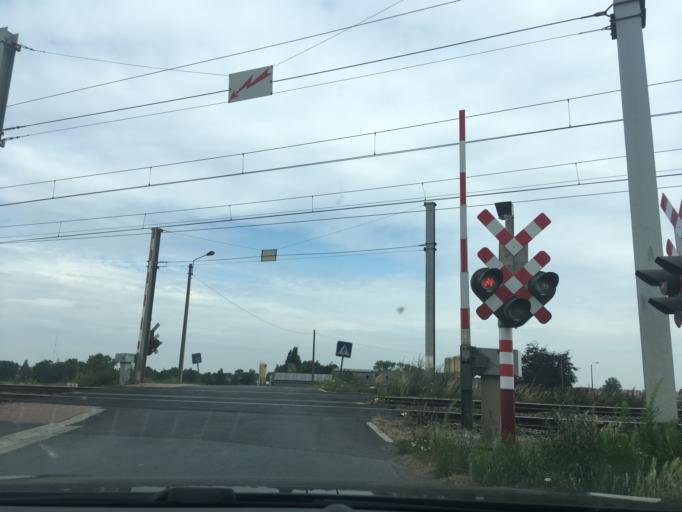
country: BE
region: Flanders
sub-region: Provincie West-Vlaanderen
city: Pittem
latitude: 50.9876
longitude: 3.2805
